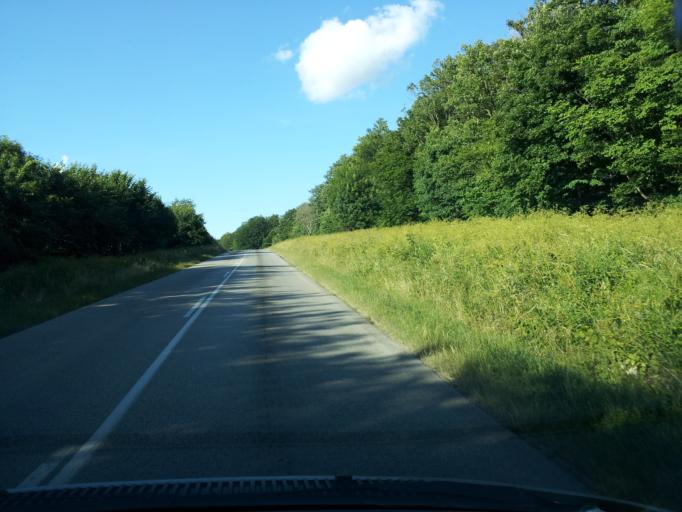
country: HU
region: Veszprem
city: Zirc
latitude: 47.2324
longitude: 17.8555
